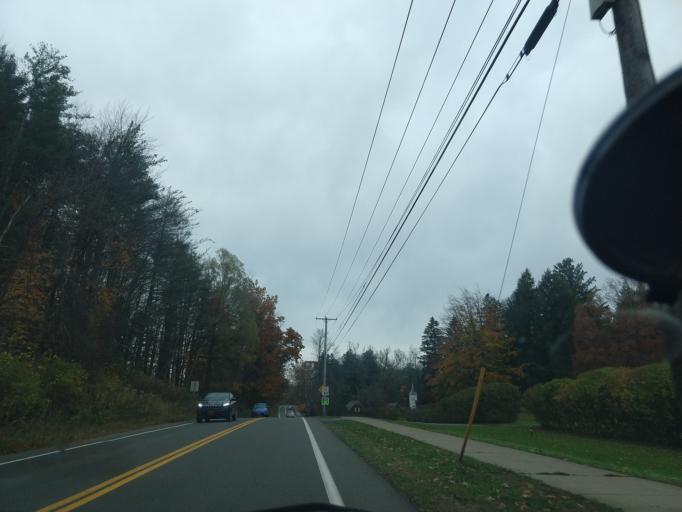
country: US
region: New York
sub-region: Tompkins County
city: Cayuga Heights
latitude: 42.4664
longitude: -76.4776
